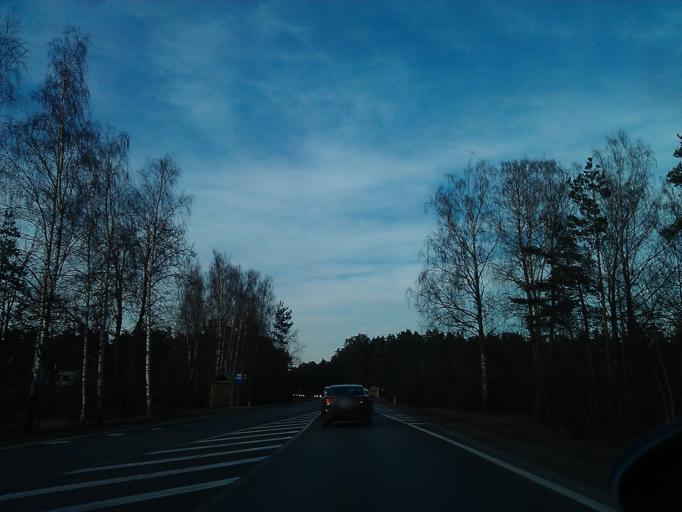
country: LV
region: Riga
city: Bergi
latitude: 57.0232
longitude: 24.3172
